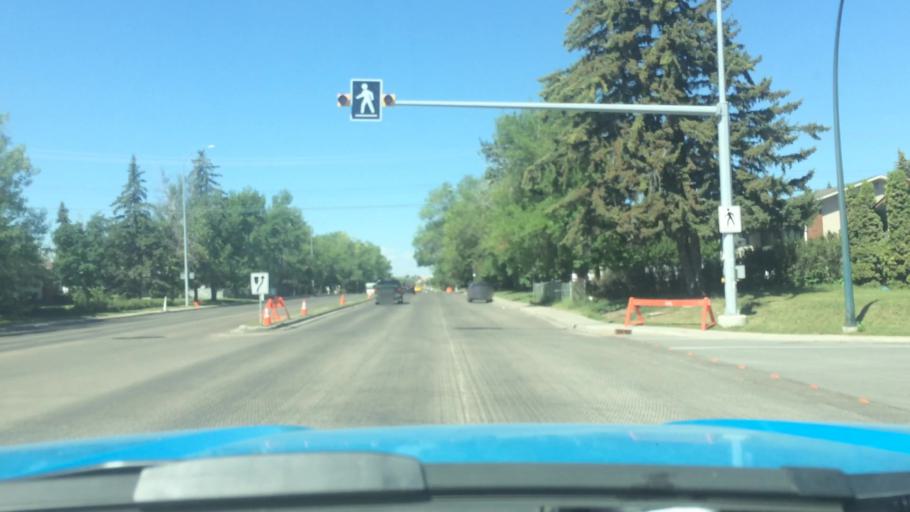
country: CA
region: Alberta
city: Calgary
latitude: 51.0529
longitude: -113.9635
